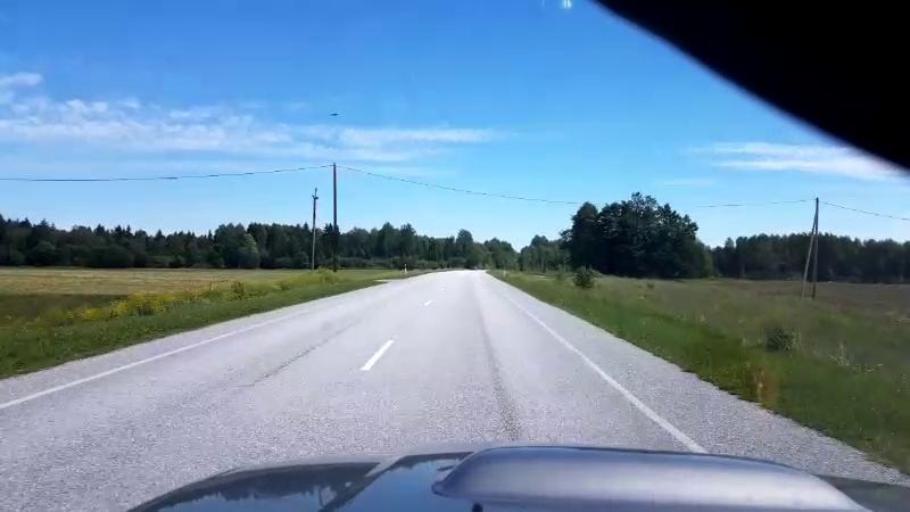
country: EE
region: Laeaene-Virumaa
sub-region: Rakke vald
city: Rakke
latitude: 58.9627
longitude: 26.1569
